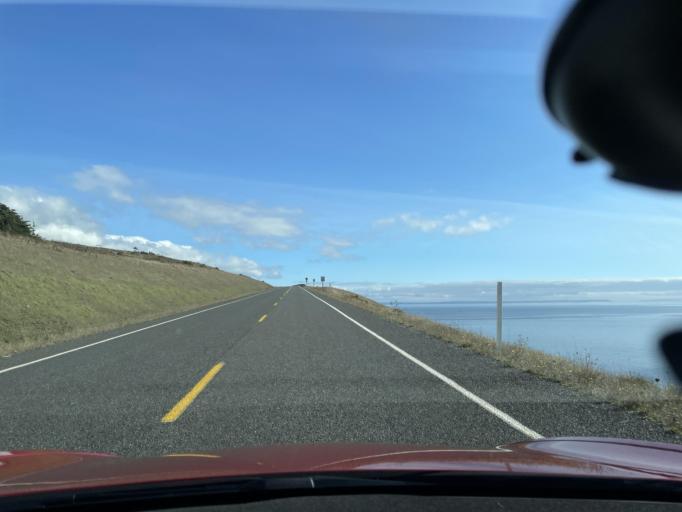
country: US
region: Washington
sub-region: San Juan County
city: Friday Harbor
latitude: 48.4562
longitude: -122.9794
